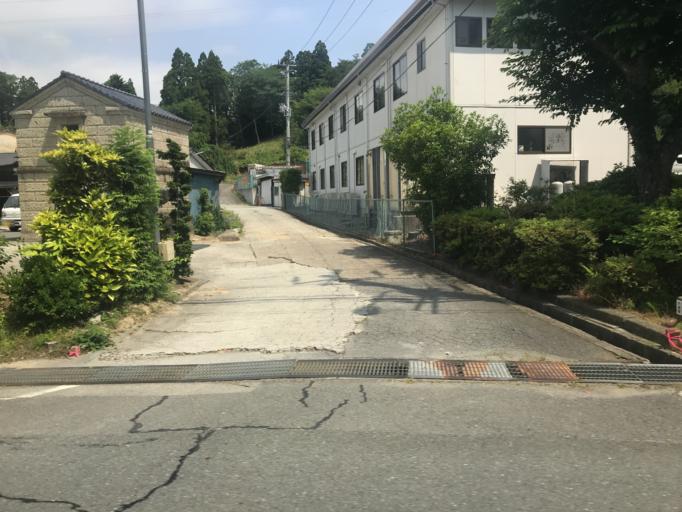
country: JP
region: Fukushima
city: Namie
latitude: 37.3148
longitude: 141.0126
